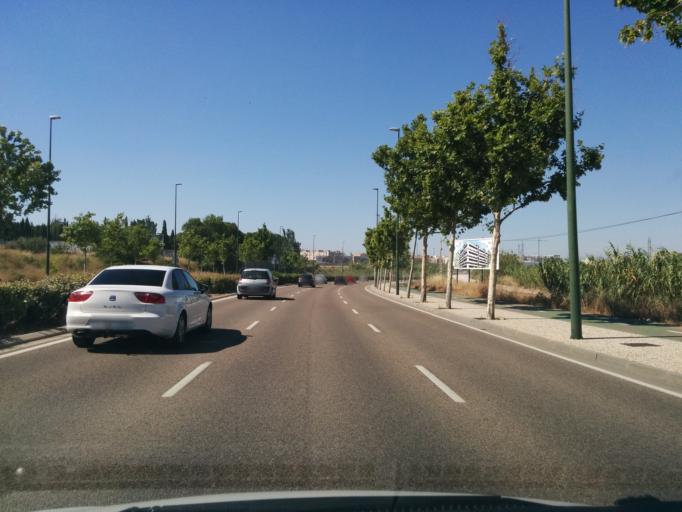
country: ES
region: Aragon
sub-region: Provincia de Zaragoza
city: Zaragoza
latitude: 41.6271
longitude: -0.8687
